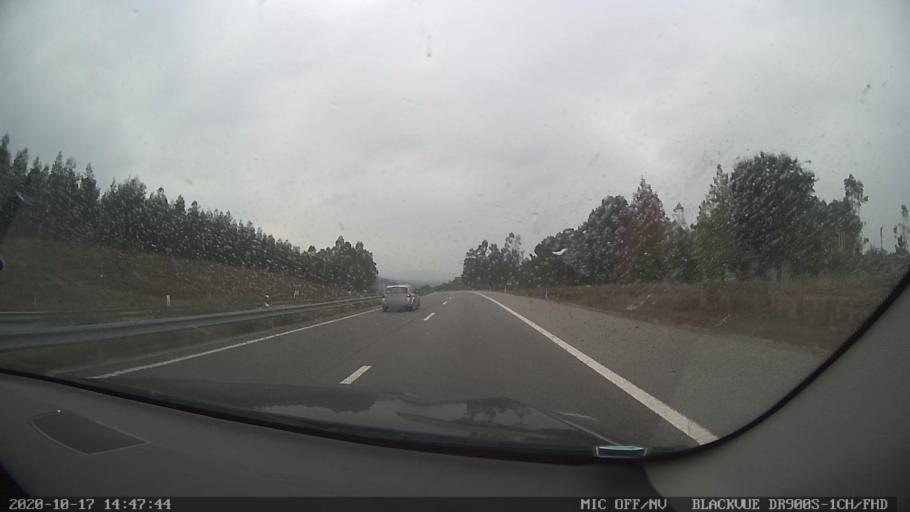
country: PT
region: Braga
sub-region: Barcelos
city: Galegos
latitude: 41.5381
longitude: -8.5292
